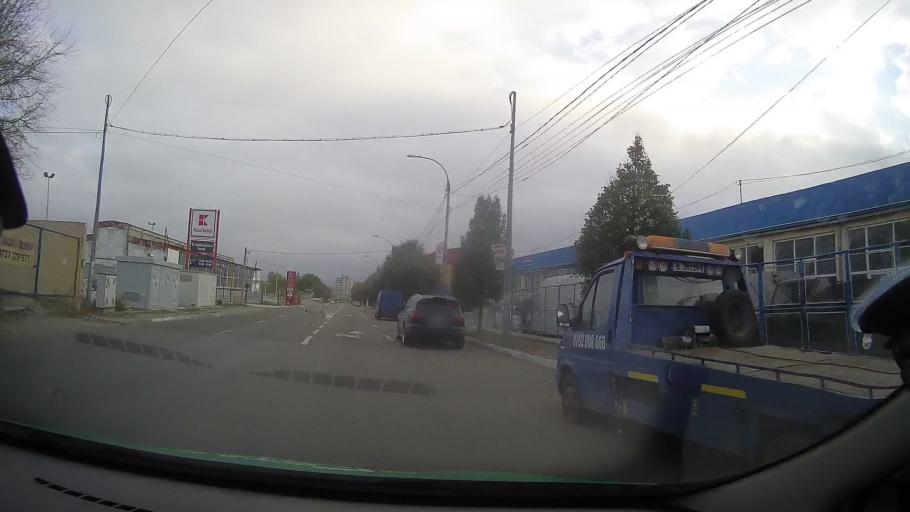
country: RO
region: Constanta
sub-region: Municipiul Medgidia
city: Medgidia
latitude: 44.2657
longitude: 28.2585
